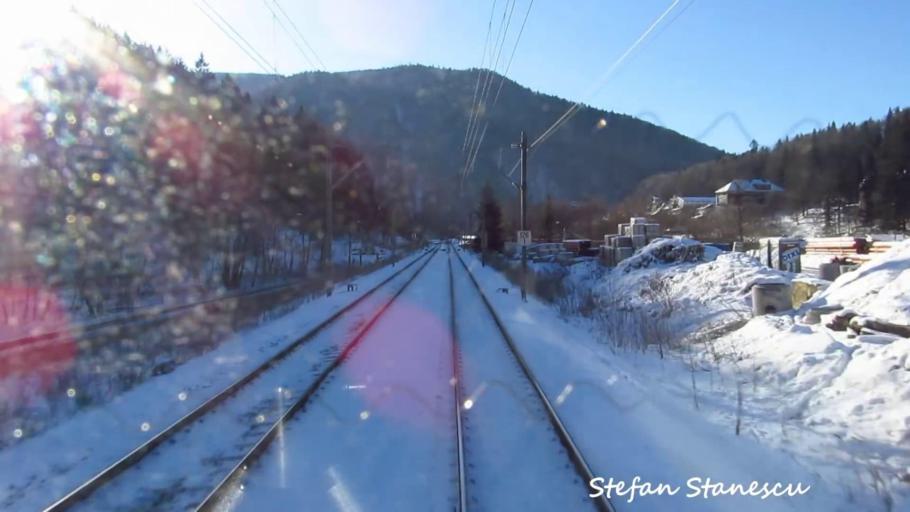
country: RO
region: Prahova
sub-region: Oras Sinaia
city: Sinaia
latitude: 45.3678
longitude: 25.5461
